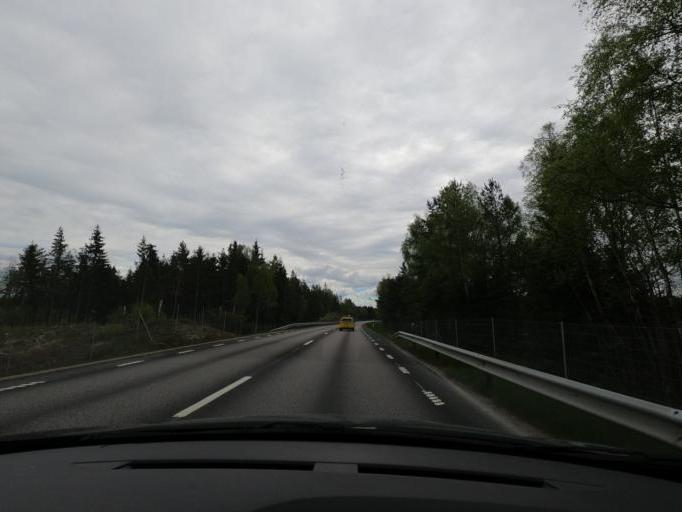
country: SE
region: Vaestra Goetaland
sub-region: Tranemo Kommun
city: Langhem
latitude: 57.5996
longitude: 13.1746
